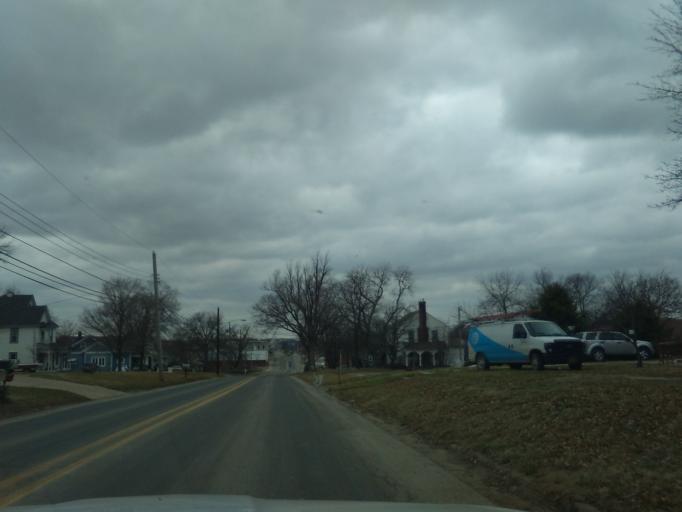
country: US
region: Nebraska
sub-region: Pawnee County
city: Pawnee City
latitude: 40.1094
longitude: -96.1487
